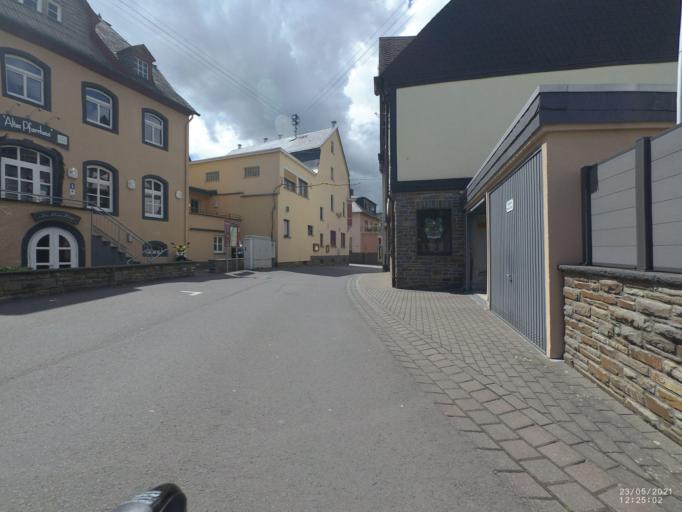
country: DE
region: Rheinland-Pfalz
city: Oberfell
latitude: 50.2591
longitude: 7.4452
